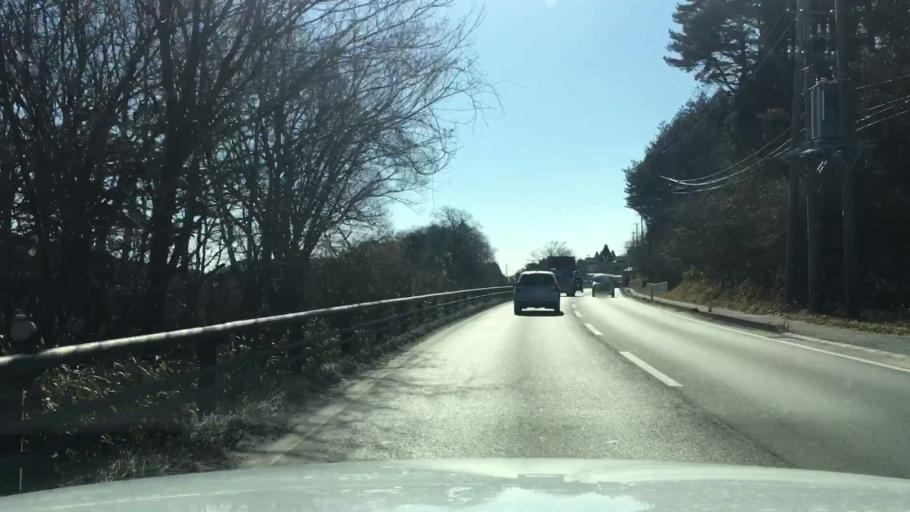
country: JP
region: Iwate
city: Yamada
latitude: 39.4425
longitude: 141.9716
